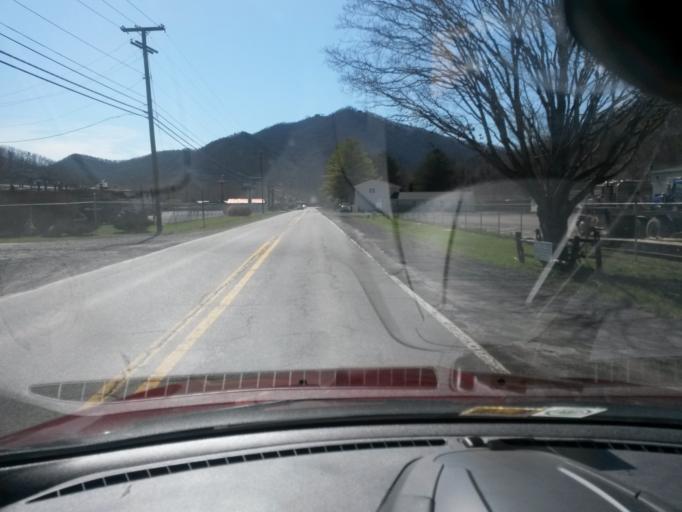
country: US
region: West Virginia
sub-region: Greenbrier County
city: White Sulphur Springs
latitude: 37.7748
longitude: -80.3483
